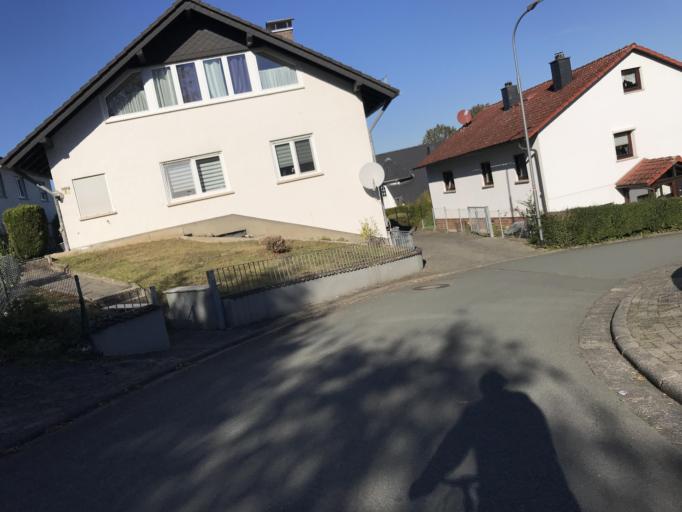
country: DE
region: Hesse
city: Solms
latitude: 50.5394
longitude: 8.4139
